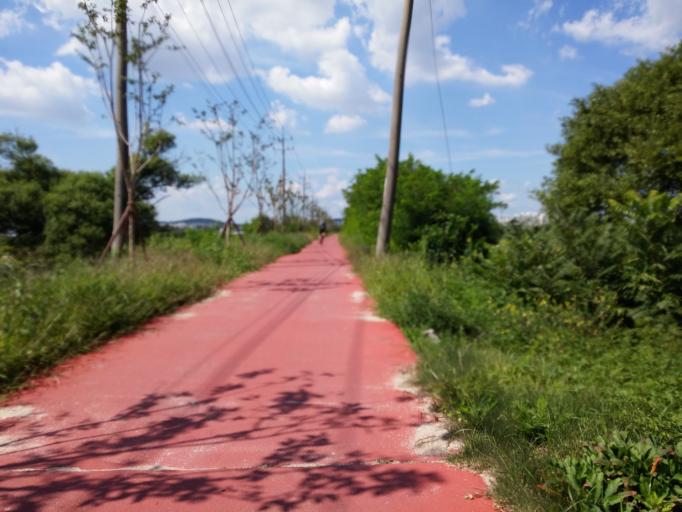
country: KR
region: Chungcheongbuk-do
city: Cheongju-si
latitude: 36.5884
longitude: 127.4990
